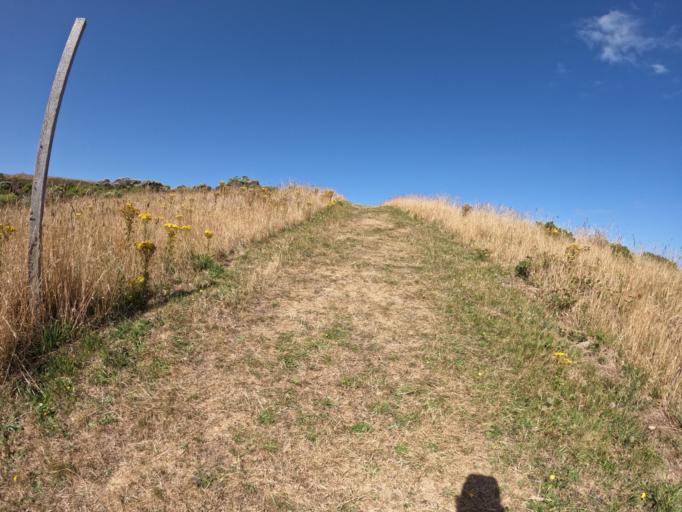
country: AU
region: Victoria
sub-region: Colac-Otway
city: Apollo Bay
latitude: -38.7905
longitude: 143.6444
